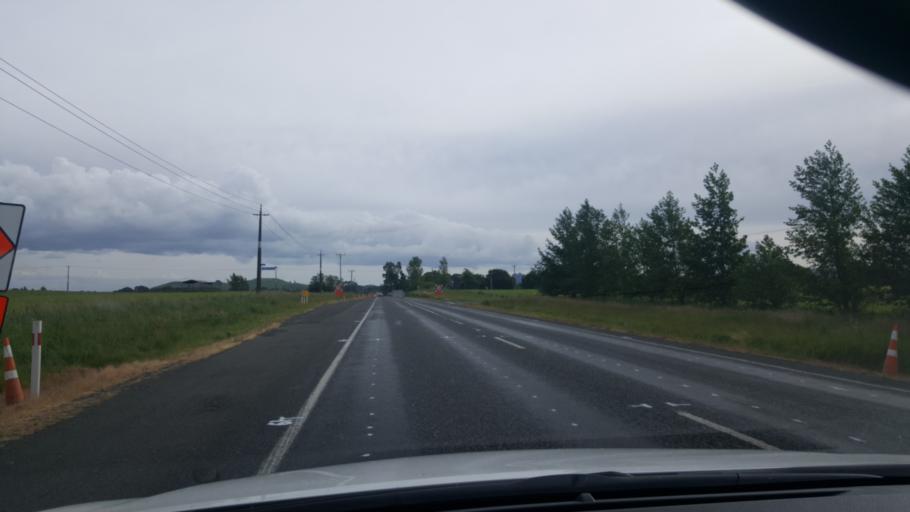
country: NZ
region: Bay of Plenty
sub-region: Rotorua District
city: Rotorua
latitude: -38.4024
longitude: 176.3298
